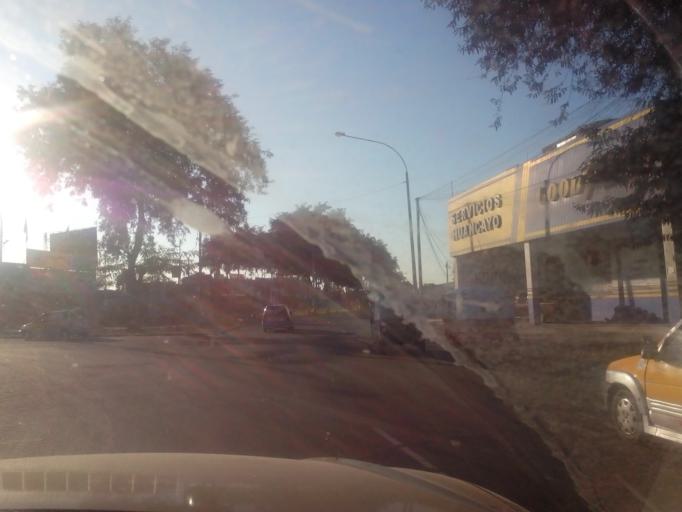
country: PE
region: Ica
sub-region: Provincia de Ica
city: Ica
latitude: -14.0662
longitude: -75.7399
